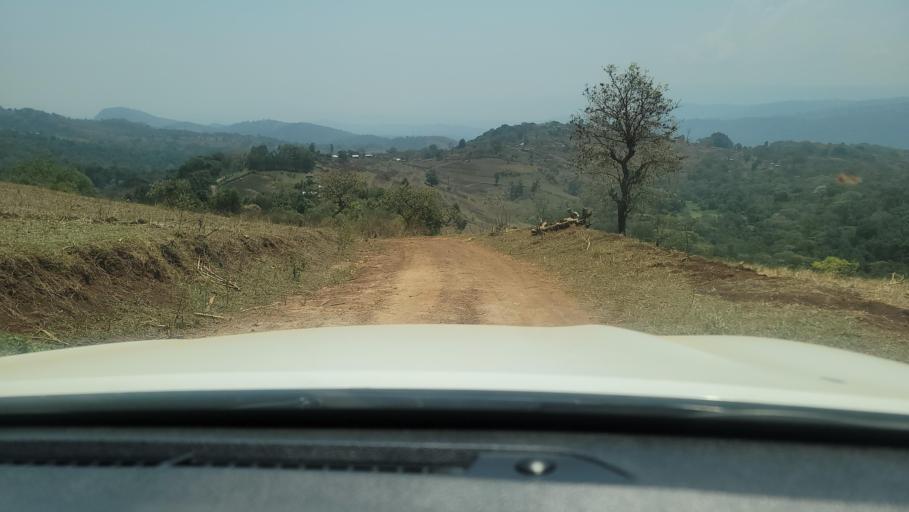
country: ET
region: Southern Nations, Nationalities, and People's Region
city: Bonga
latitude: 7.5286
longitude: 36.1924
